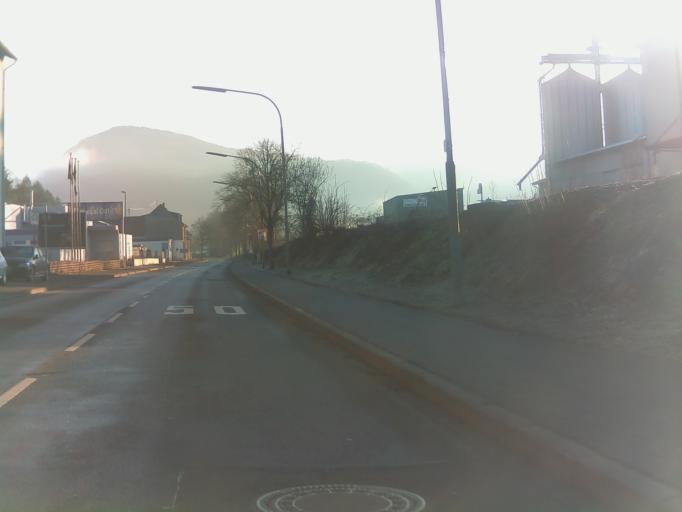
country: DE
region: Rheinland-Pfalz
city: Kirn
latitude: 49.7881
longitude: 7.4729
